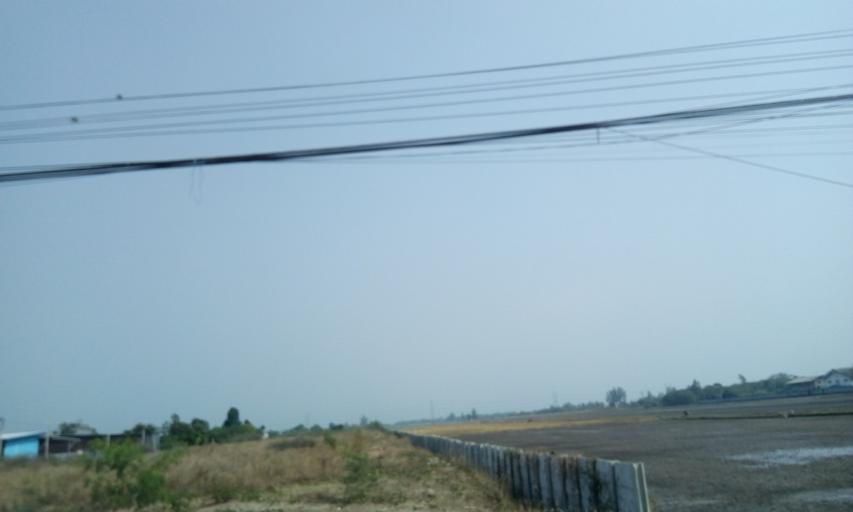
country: TH
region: Pathum Thani
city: Ban Lam Luk Ka
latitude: 13.9742
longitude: 100.7525
